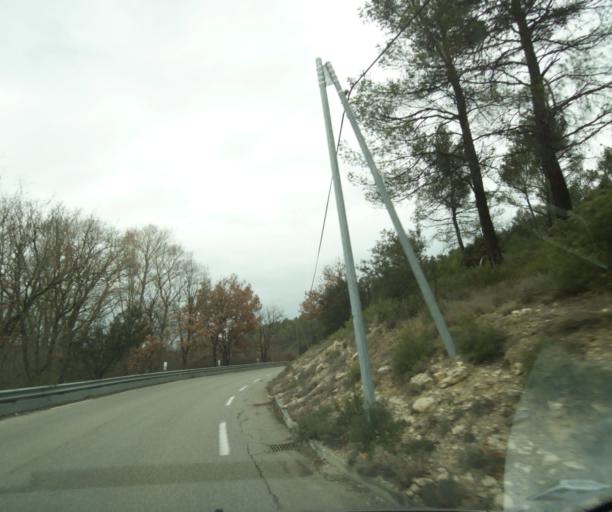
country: FR
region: Provence-Alpes-Cote d'Azur
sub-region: Departement des Bouches-du-Rhone
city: Jouques
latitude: 43.6256
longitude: 5.6664
